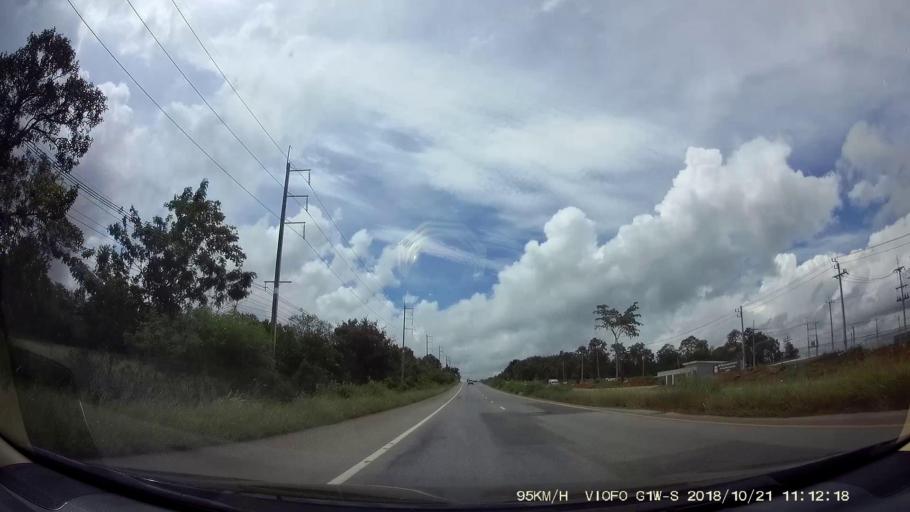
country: TH
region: Chaiyaphum
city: Khon Sawan
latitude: 15.9297
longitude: 102.1457
